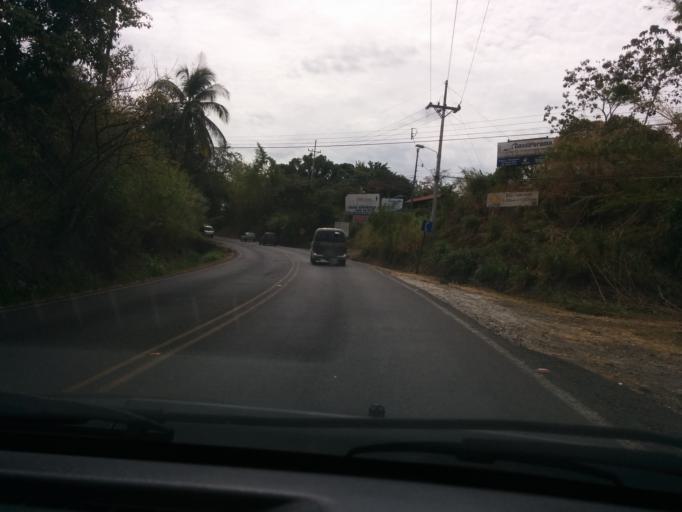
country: CR
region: Puntarenas
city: Esparza
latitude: 9.9992
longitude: -84.6756
